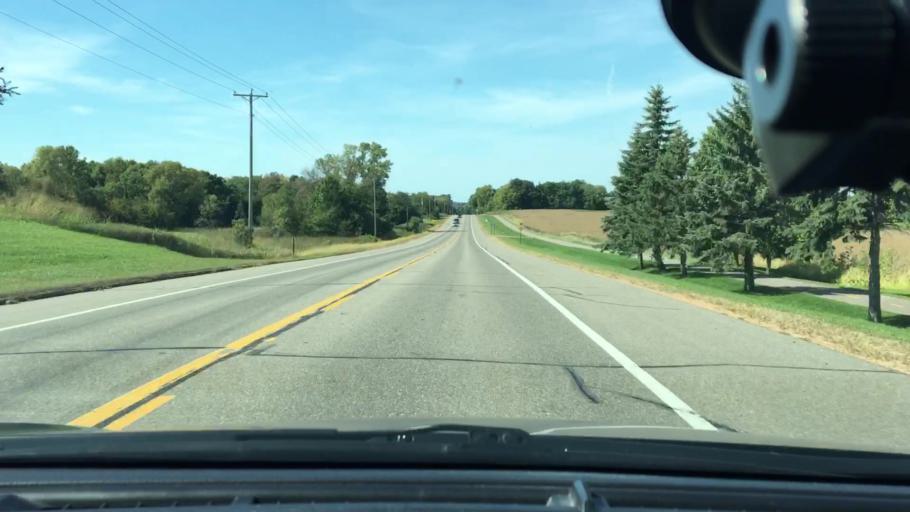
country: US
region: Minnesota
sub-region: Wright County
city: Hanover
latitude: 45.1525
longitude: -93.6497
